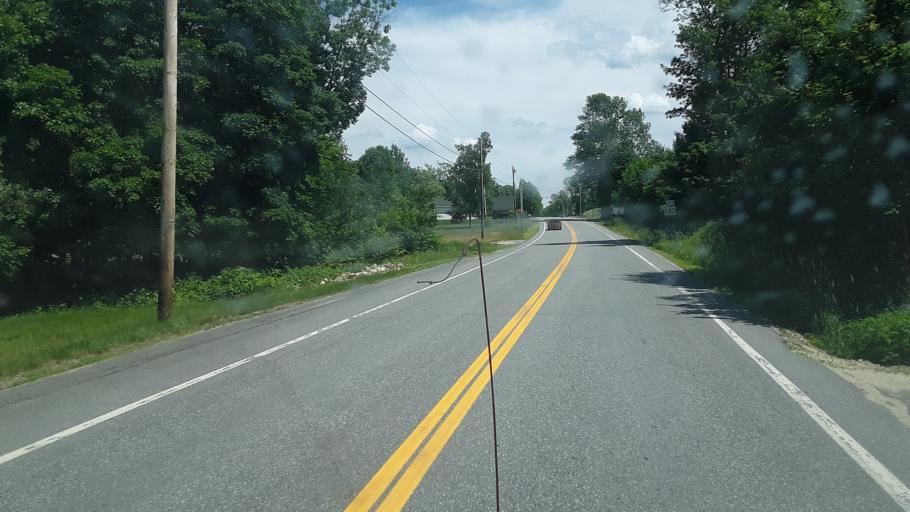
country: US
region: Maine
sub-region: Franklin County
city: Wilton
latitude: 44.5786
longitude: -70.1782
